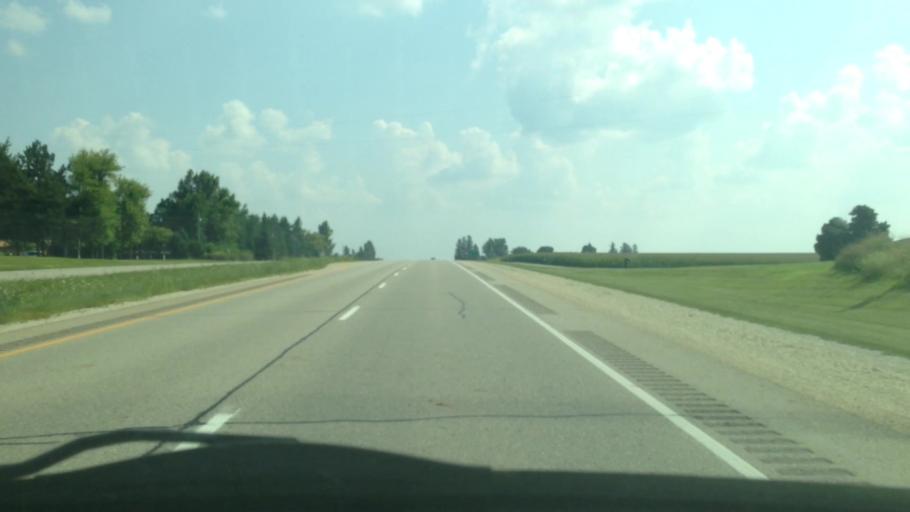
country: US
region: Iowa
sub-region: Bremer County
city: Denver
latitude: 42.6346
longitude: -92.3377
